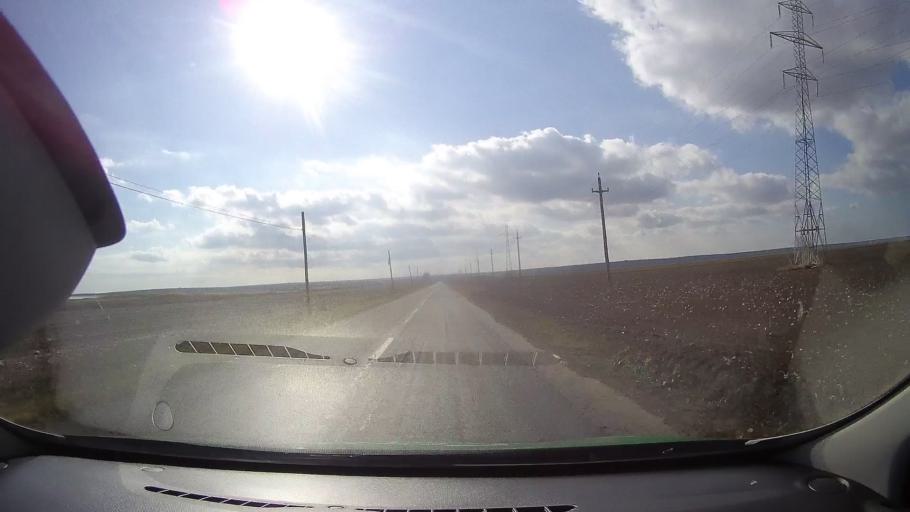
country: RO
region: Constanta
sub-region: Comuna Istria
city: Istria
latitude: 44.5414
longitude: 28.6899
